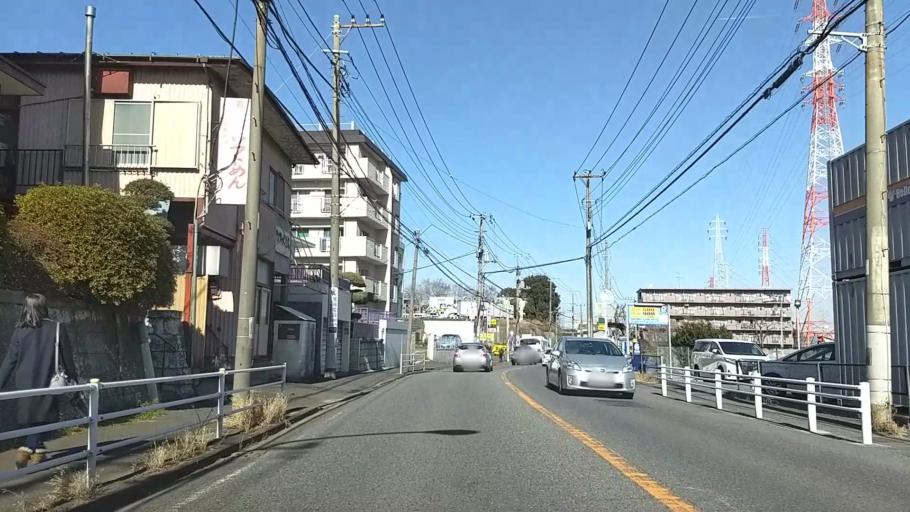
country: JP
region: Kanagawa
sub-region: Kawasaki-shi
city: Kawasaki
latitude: 35.5200
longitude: 139.6496
